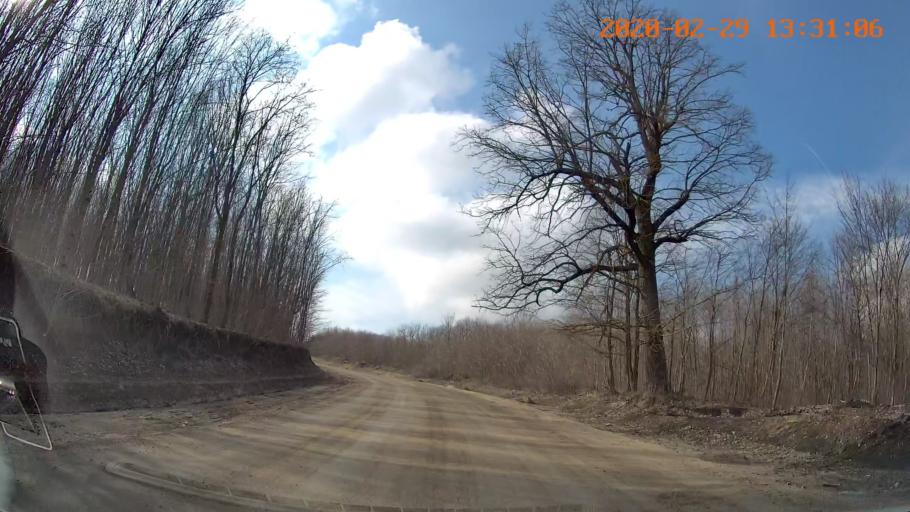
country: MD
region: Telenesti
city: Camenca
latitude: 47.8828
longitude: 28.6225
